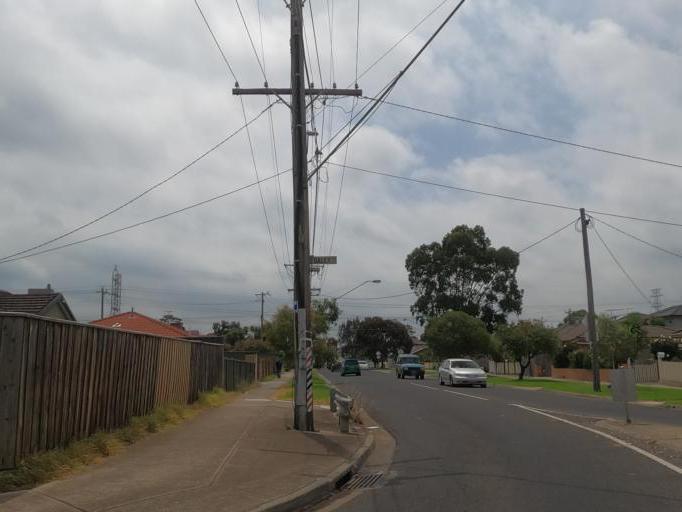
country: AU
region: Victoria
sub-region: Moreland
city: Glenroy
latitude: -37.6966
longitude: 144.9248
